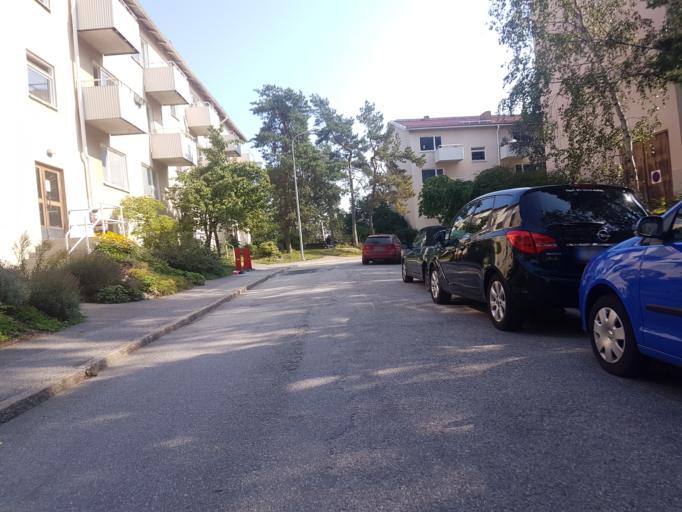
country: SE
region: Stockholm
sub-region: Stockholms Kommun
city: OEstermalm
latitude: 59.2972
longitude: 18.1138
